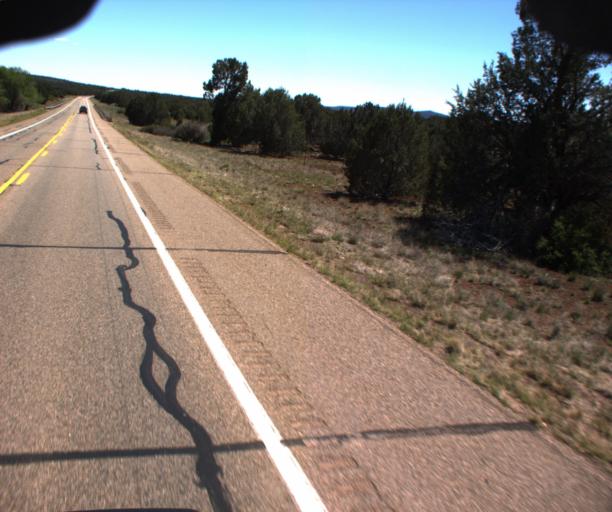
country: US
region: Arizona
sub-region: Yavapai County
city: Paulden
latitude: 35.1311
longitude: -112.4387
